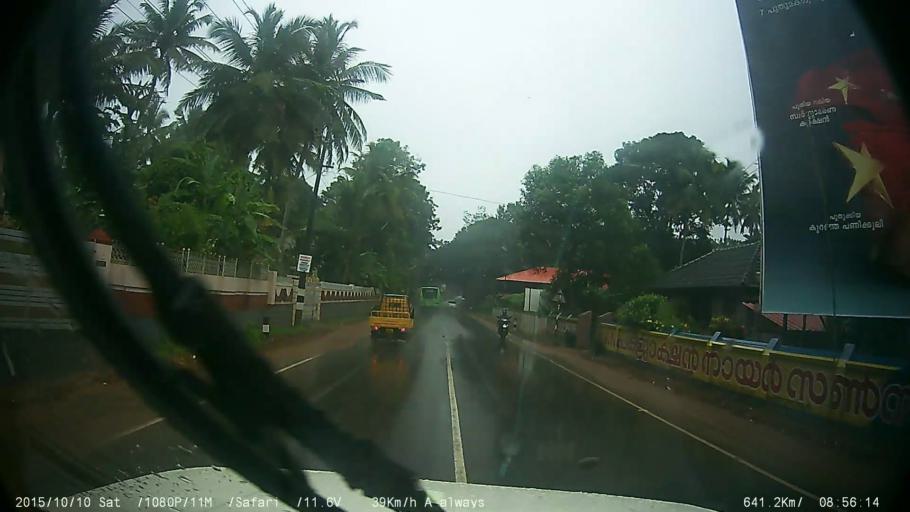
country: IN
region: Kerala
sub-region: Kottayam
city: Palackattumala
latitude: 9.6956
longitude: 76.5495
